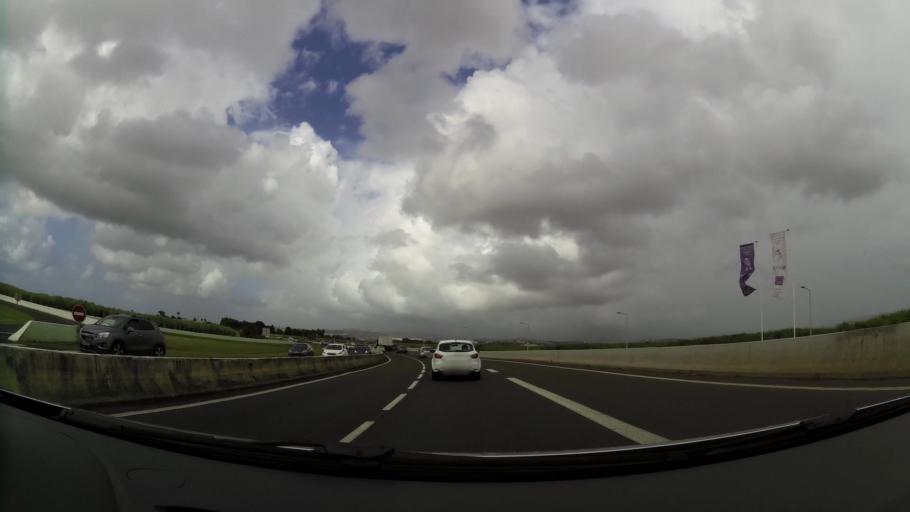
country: MQ
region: Martinique
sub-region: Martinique
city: Ducos
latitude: 14.5954
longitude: -60.9849
